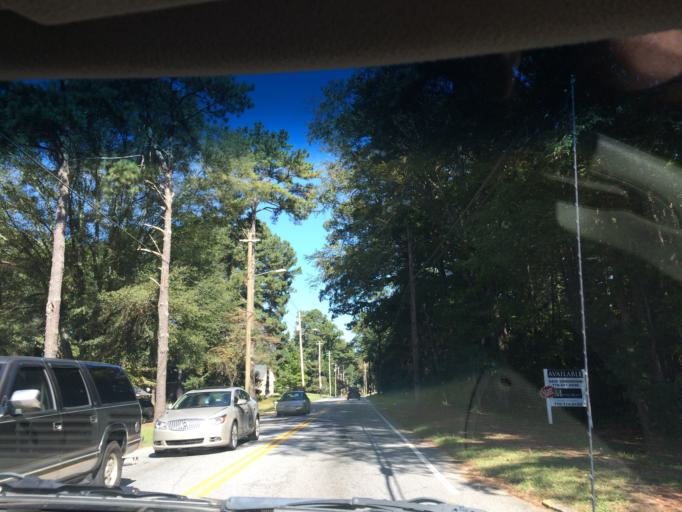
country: US
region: Georgia
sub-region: Fulton County
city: College Park
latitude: 33.6604
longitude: -84.4760
